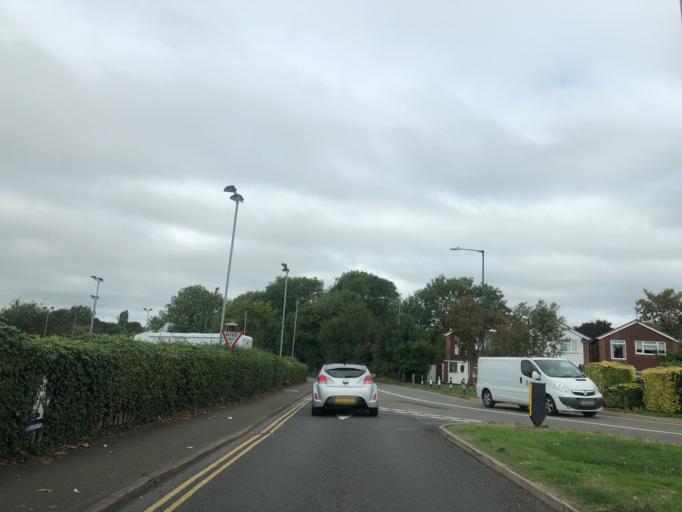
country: GB
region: England
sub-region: Warwickshire
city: Warwick
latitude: 52.2907
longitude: -1.5833
